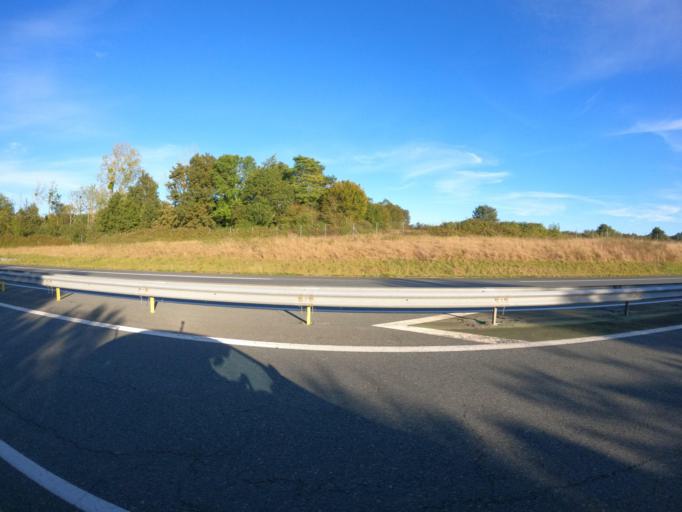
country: FR
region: Pays de la Loire
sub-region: Departement de Maine-et-Loire
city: Mazieres-en-Mauges
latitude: 47.0789
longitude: -0.8256
